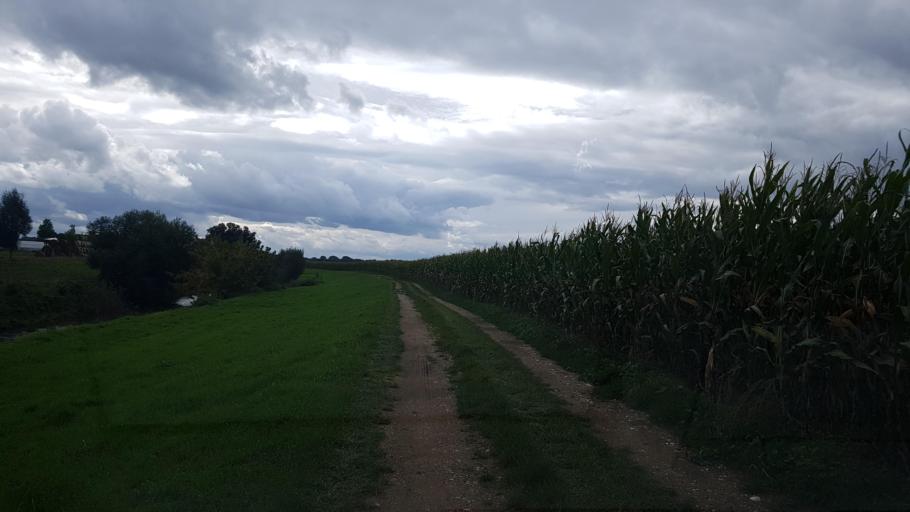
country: DE
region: Saxony
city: Pegau
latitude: 51.1495
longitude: 12.2581
